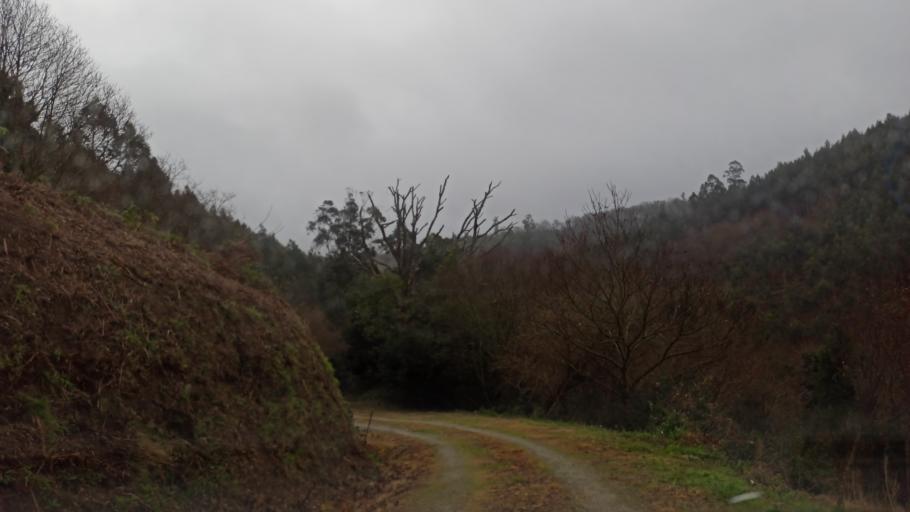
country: ES
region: Galicia
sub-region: Provincia da Coruna
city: Cesuras
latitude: 43.1763
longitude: -8.1567
